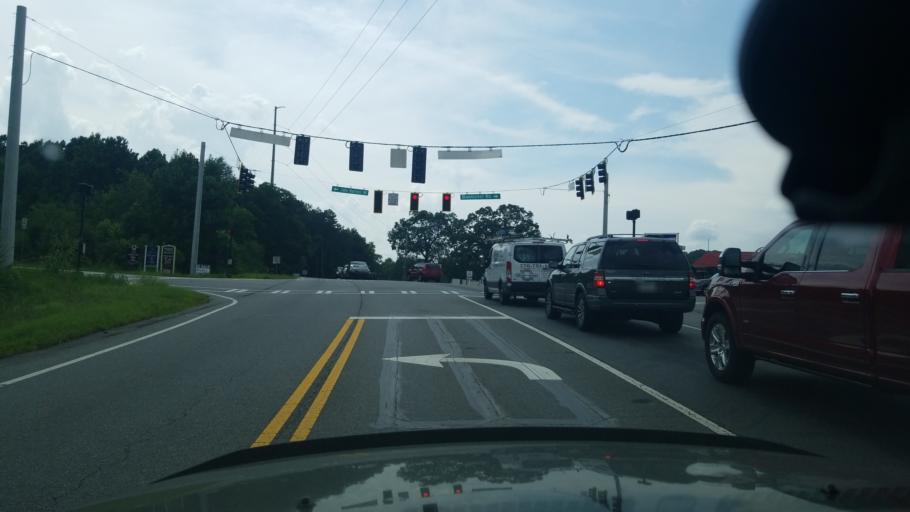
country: US
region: Georgia
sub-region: Forsyth County
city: Cumming
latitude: 34.2987
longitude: -84.1529
